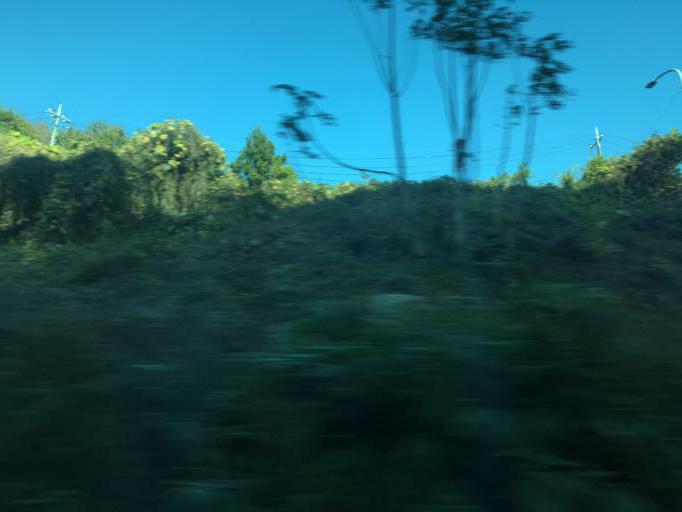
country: JP
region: Ibaraki
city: Iwase
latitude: 36.3501
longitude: 140.1664
